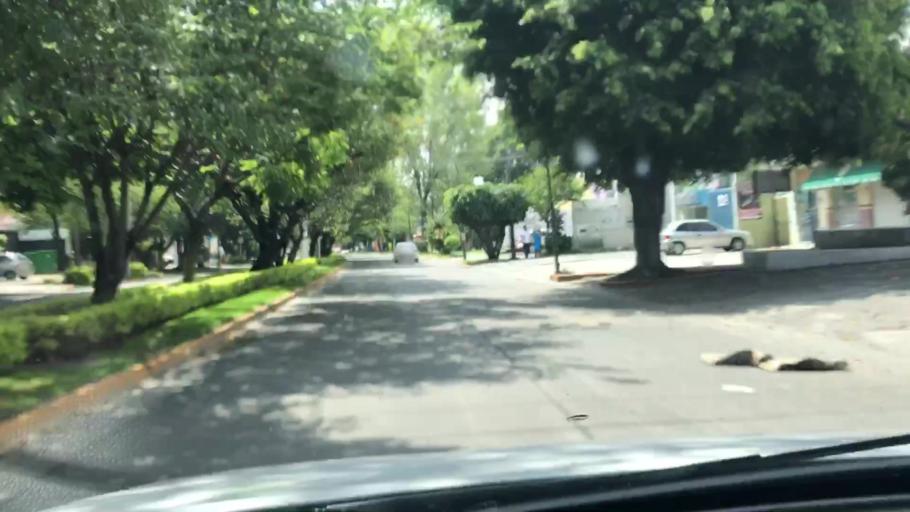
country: MX
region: Jalisco
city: Guadalajara
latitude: 20.6631
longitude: -103.4013
